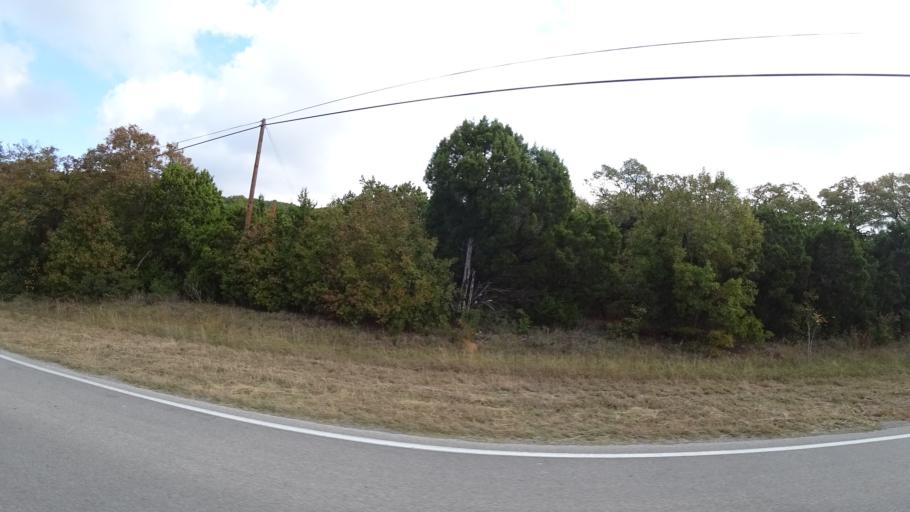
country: US
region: Texas
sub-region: Travis County
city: Hudson Bend
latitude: 30.4169
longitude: -97.8689
